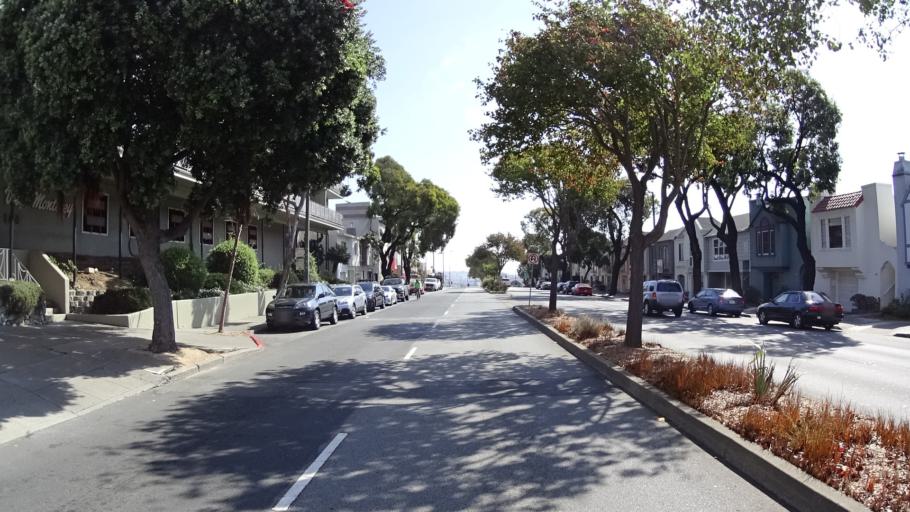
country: US
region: California
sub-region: San Mateo County
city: Daly City
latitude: 37.7316
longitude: -122.4391
